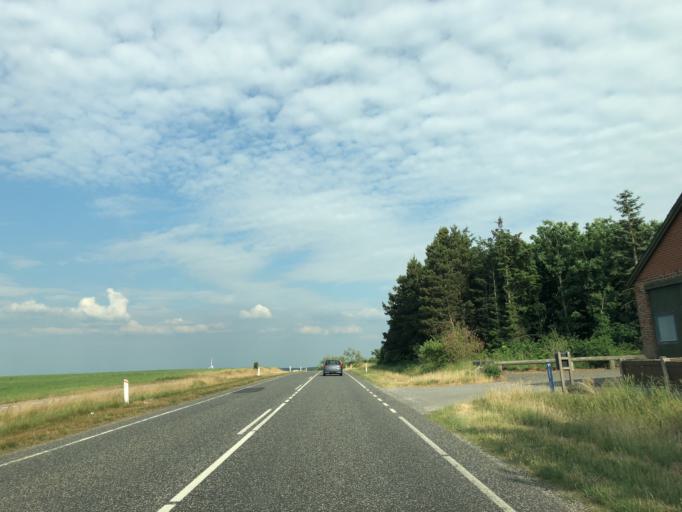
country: DK
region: Central Jutland
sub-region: Ringkobing-Skjern Kommune
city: Skjern
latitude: 55.9001
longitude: 8.4626
